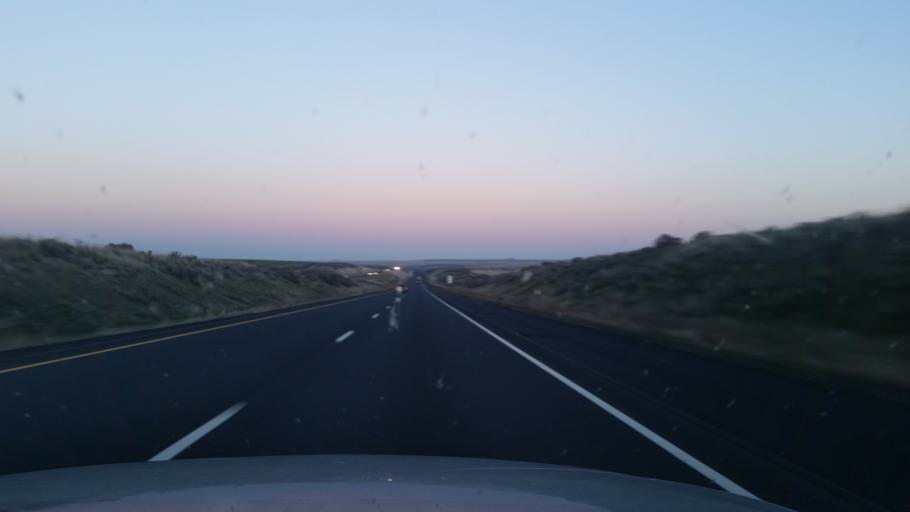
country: US
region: Washington
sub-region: Adams County
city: Ritzville
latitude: 47.0966
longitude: -118.6528
